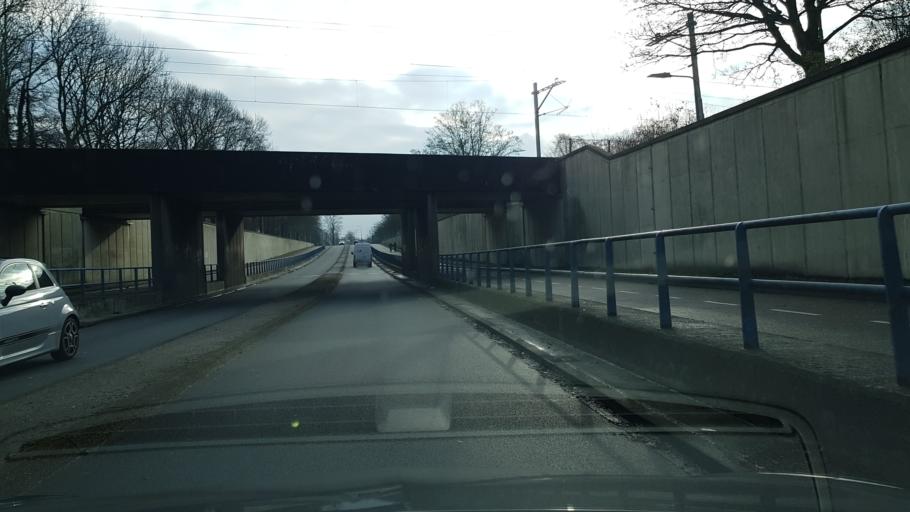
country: NL
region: North Holland
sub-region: Gemeente Velsen
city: Velsen-Zuid
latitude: 52.4437
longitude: 4.6395
